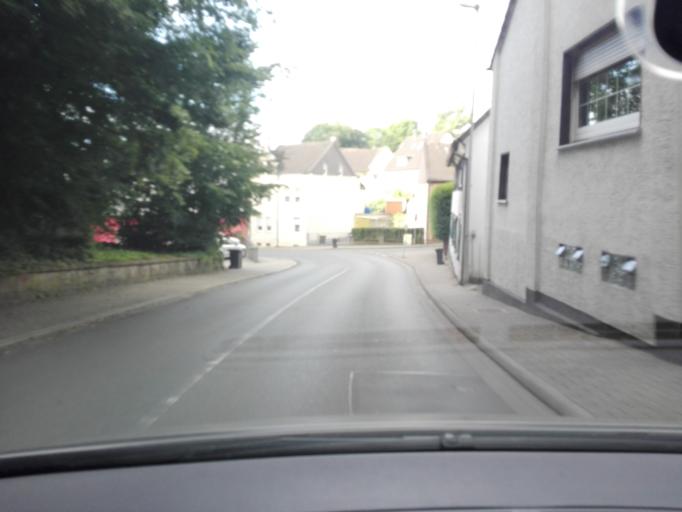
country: DE
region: North Rhine-Westphalia
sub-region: Regierungsbezirk Arnsberg
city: Frondenberg
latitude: 51.4752
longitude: 7.7672
